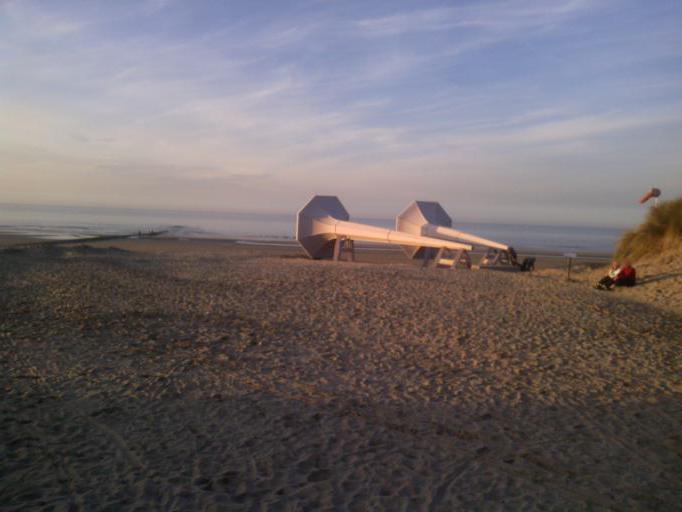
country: BE
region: Flanders
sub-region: Provincie West-Vlaanderen
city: Middelkerke
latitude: 51.1756
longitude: 2.7857
